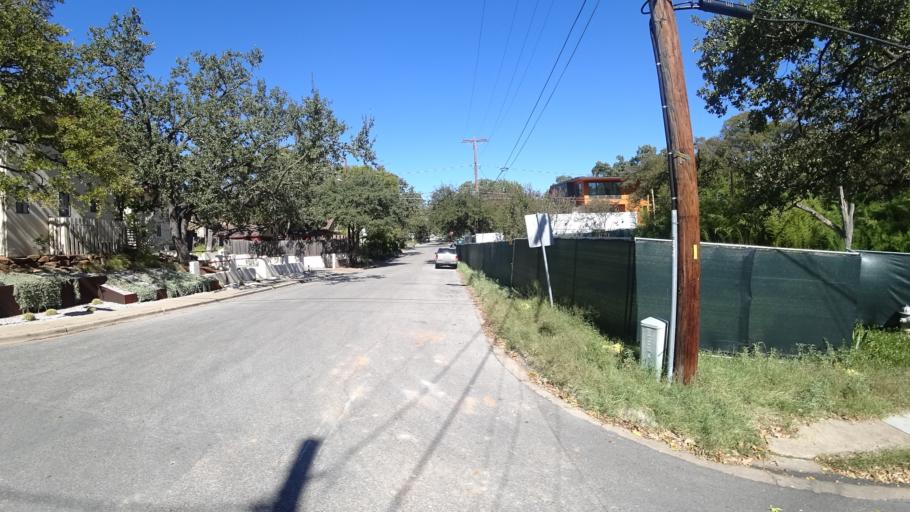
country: US
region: Texas
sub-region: Travis County
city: Austin
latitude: 30.2820
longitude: -97.7613
